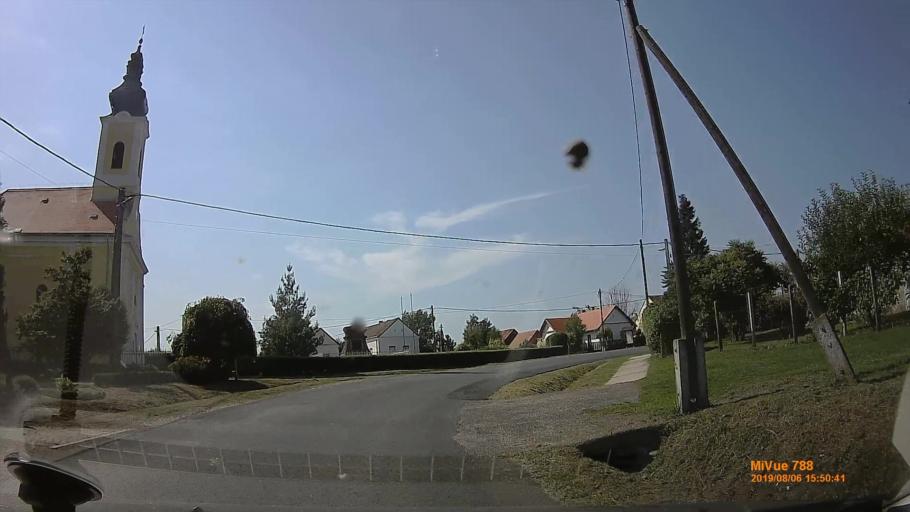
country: HU
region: Somogy
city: Csurgo
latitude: 46.2728
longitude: 17.0402
